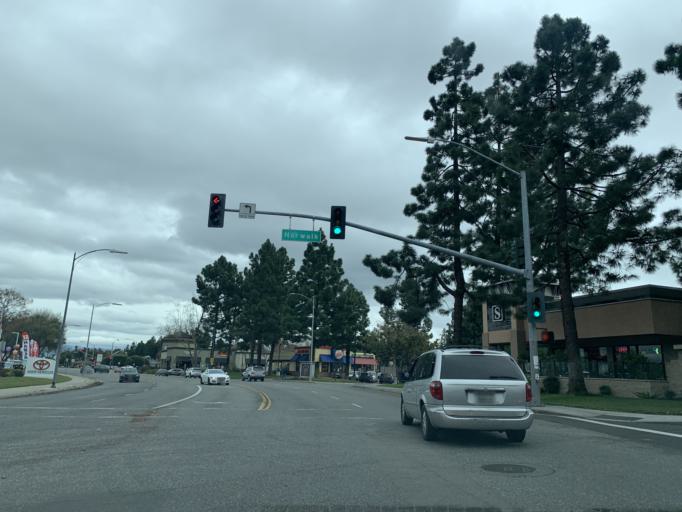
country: US
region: California
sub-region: Santa Clara County
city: Santa Clara
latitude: 37.3201
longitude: -121.9732
